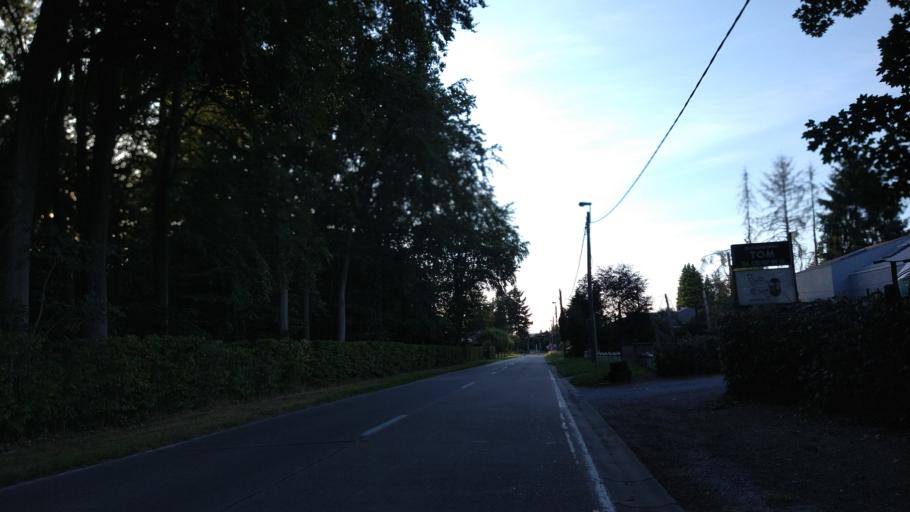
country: BE
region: Flanders
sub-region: Provincie Vlaams-Brabant
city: Bertem
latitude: 50.8394
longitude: 4.5958
